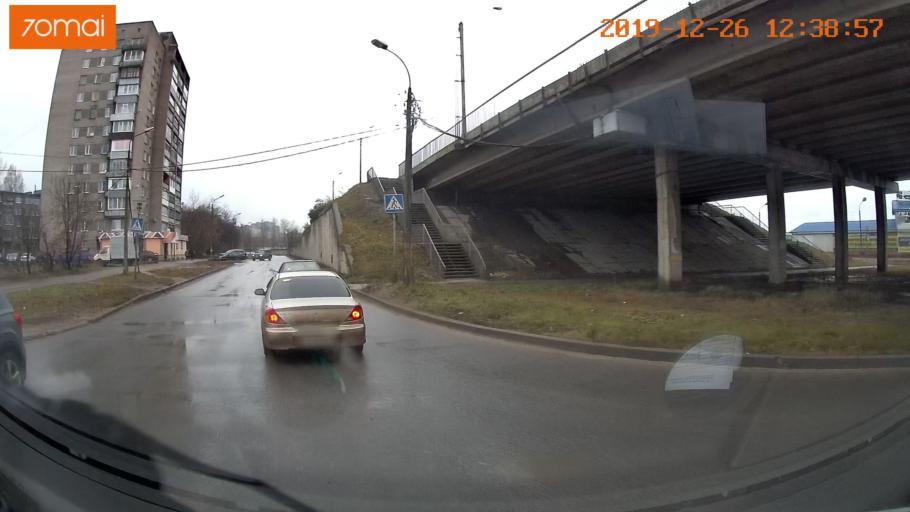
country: RU
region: Vologda
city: Tonshalovo
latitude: 59.1357
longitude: 37.9785
